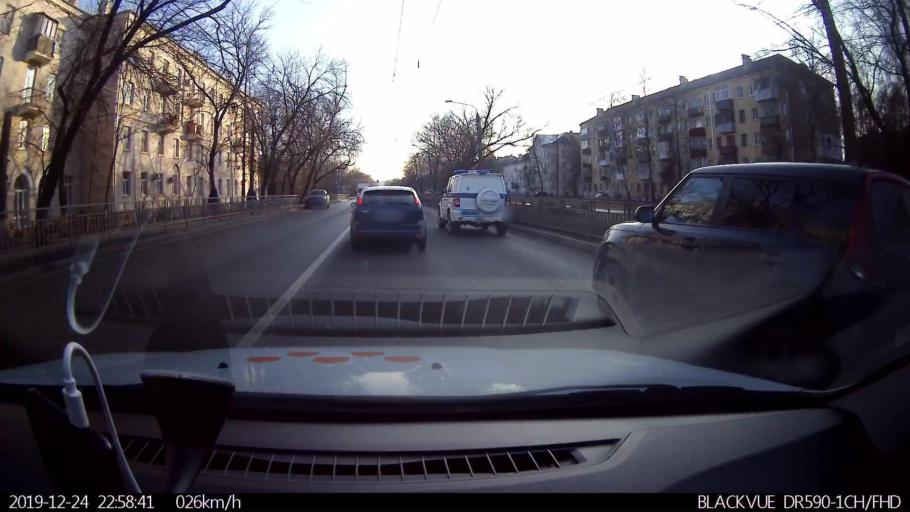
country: RU
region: Nizjnij Novgorod
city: Nizhniy Novgorod
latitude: 56.2798
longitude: 43.9324
